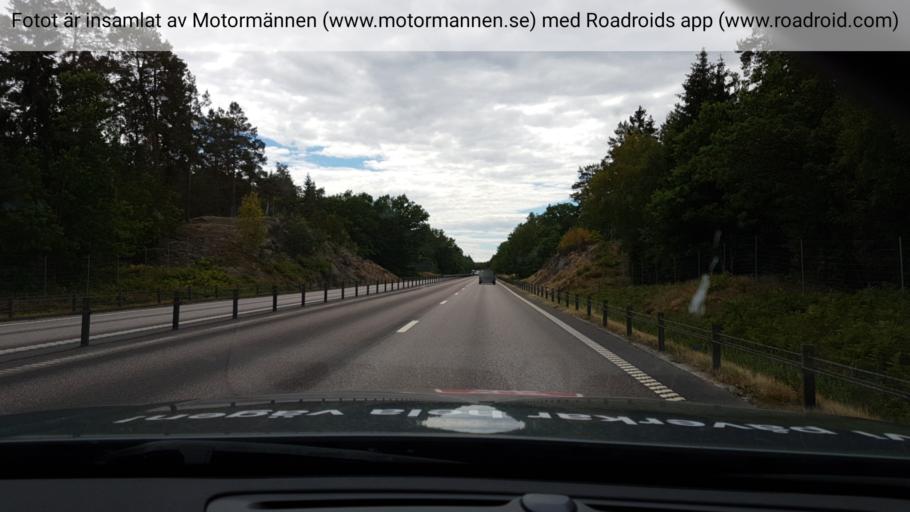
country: SE
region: Kalmar
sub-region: Oskarshamns Kommun
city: Paskallavik
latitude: 57.1757
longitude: 16.4442
